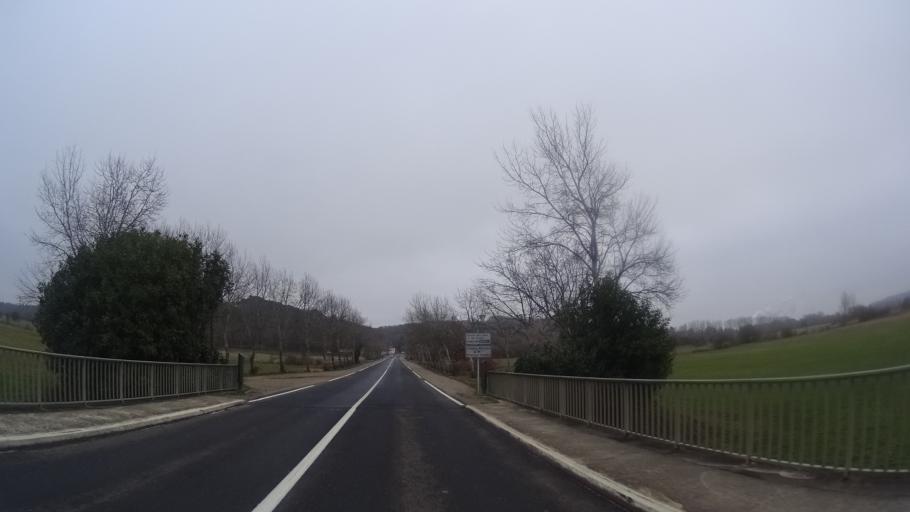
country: FR
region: Brittany
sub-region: Departement du Morbihan
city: Saint-Perreux
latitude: 47.6646
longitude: -2.1038
